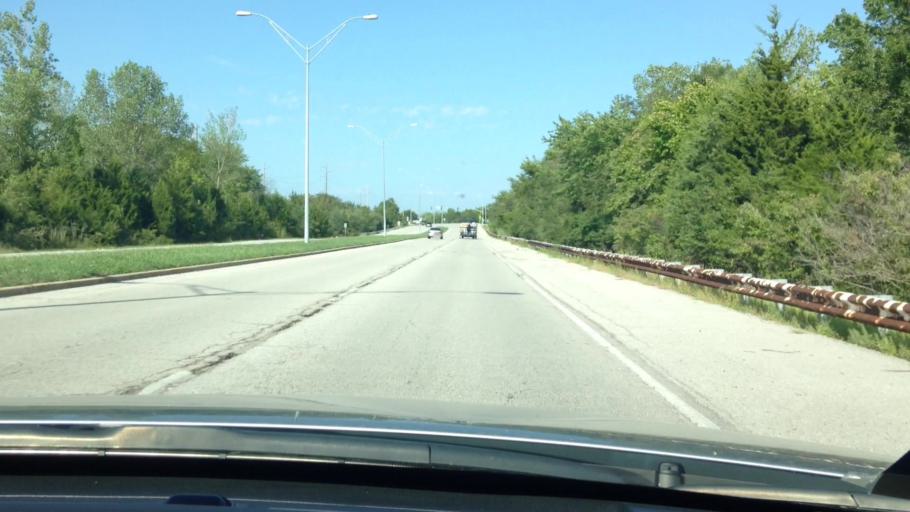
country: US
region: Missouri
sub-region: Jackson County
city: Grandview
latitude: 38.9197
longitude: -94.4788
